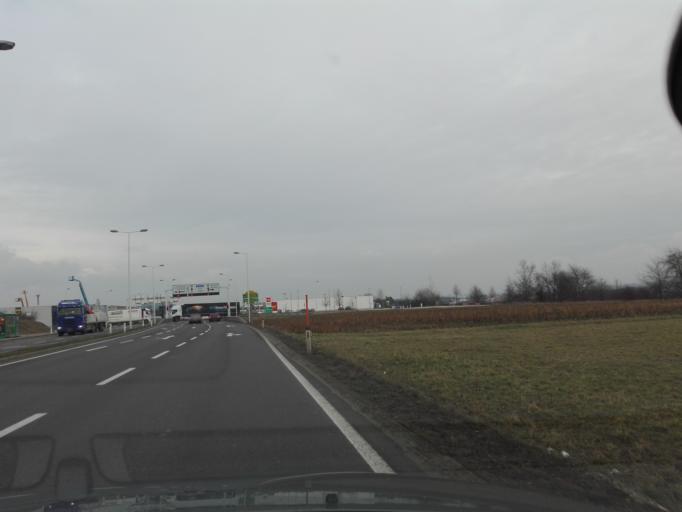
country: AT
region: Upper Austria
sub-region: Politischer Bezirk Linz-Land
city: Horsching
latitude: 48.2130
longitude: 14.1795
